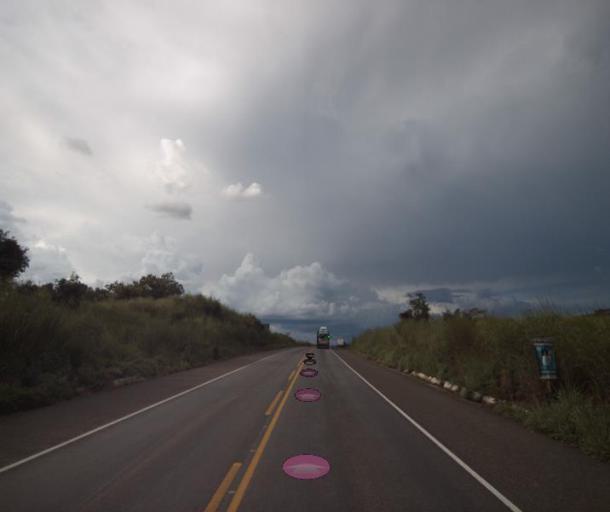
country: BR
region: Goias
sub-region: Ceres
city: Ceres
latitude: -15.2270
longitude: -49.5542
